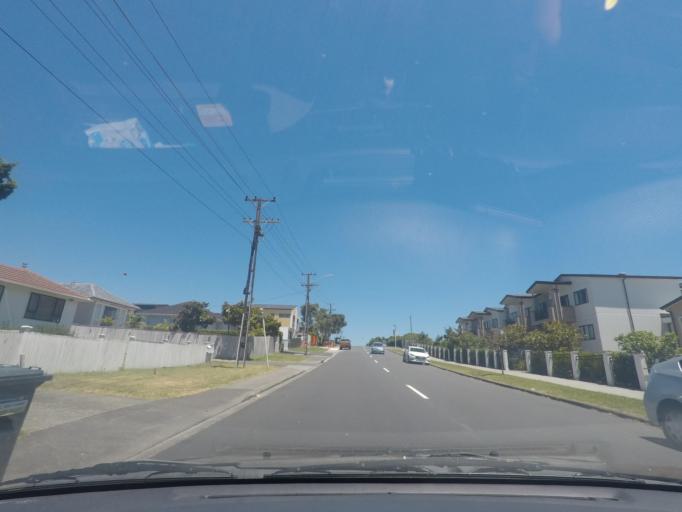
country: NZ
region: Auckland
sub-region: Auckland
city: Waitakere
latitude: -36.9191
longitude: 174.7142
